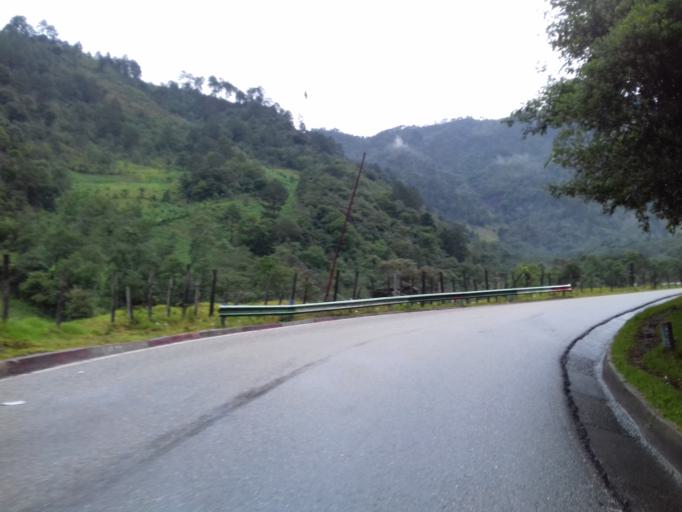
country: GT
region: Quiche
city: Nebaj
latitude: 15.3870
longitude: -91.1144
